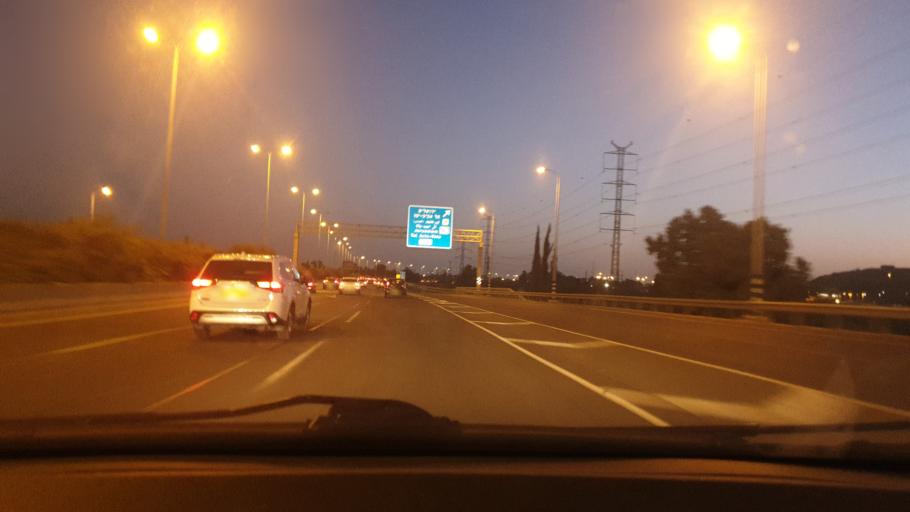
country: IL
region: Tel Aviv
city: Azor
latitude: 32.0346
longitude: 34.8291
